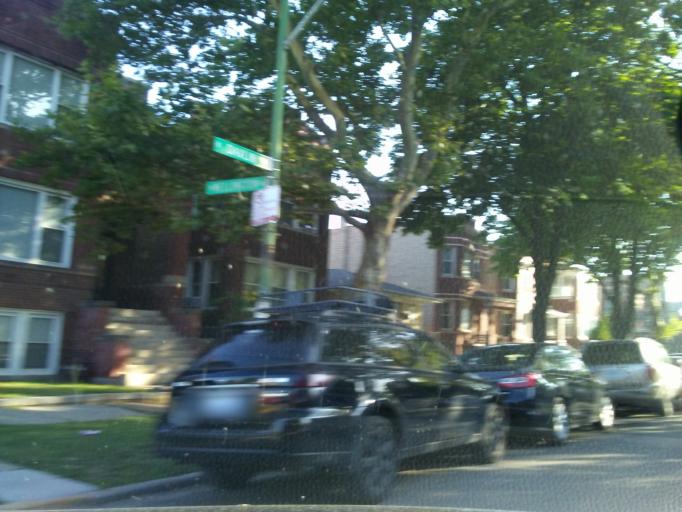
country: US
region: Illinois
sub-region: Cook County
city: Lincolnwood
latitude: 41.9355
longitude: -87.7262
